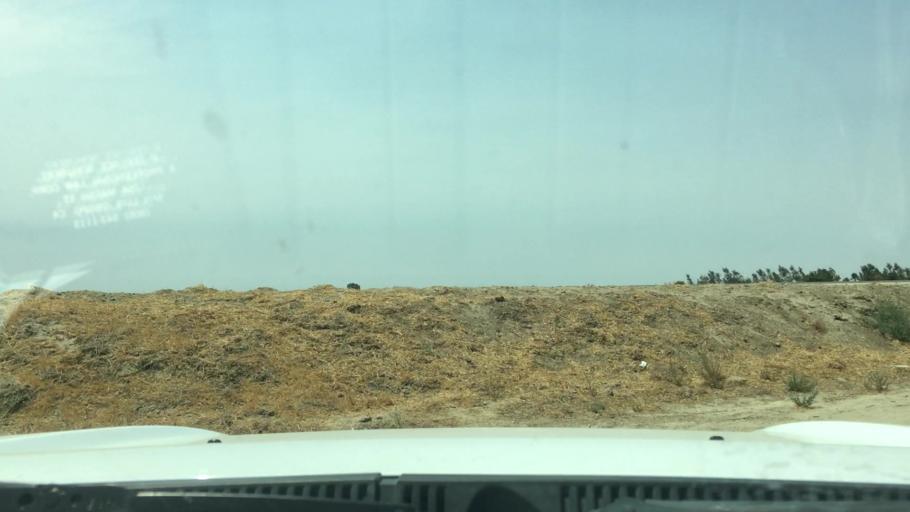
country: US
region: California
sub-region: Kern County
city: Wasco
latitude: 35.6813
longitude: -119.4371
